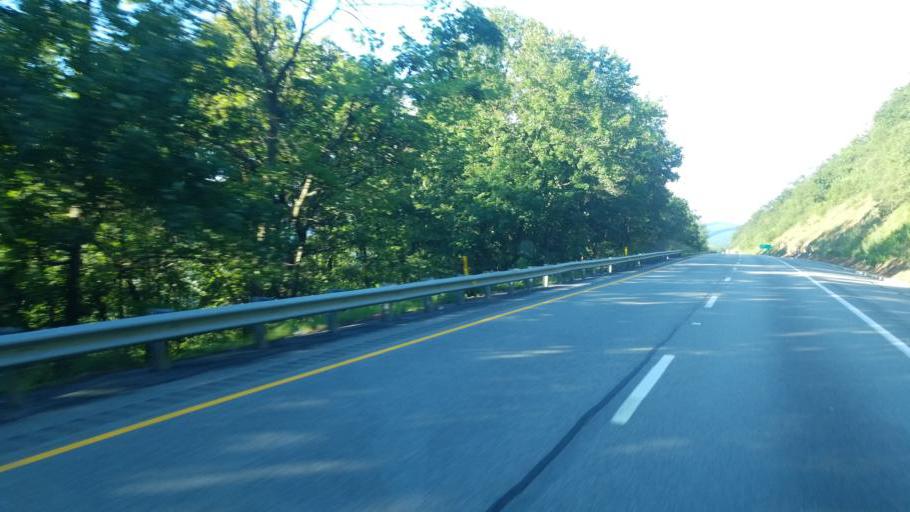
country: US
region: Pennsylvania
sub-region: Bedford County
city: Earlston
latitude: 39.8795
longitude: -78.2469
